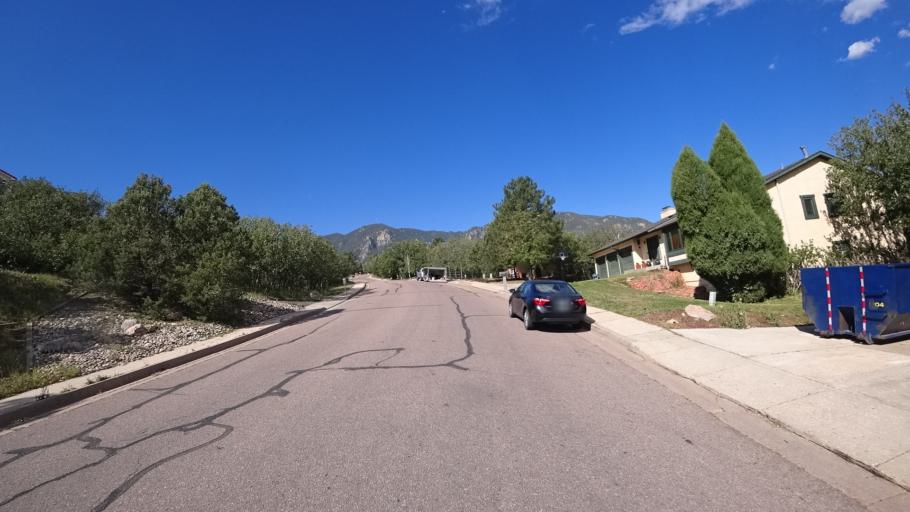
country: US
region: Colorado
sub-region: El Paso County
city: Stratmoor
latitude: 38.7668
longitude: -104.8221
